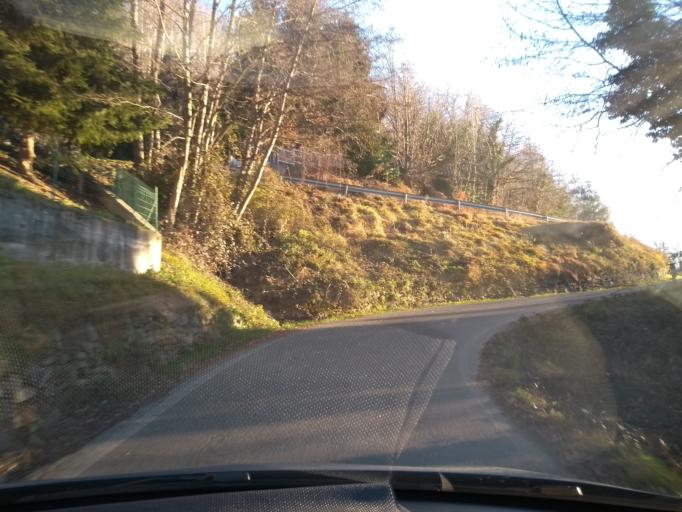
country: IT
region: Piedmont
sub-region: Provincia di Torino
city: Corio
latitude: 45.3206
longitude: 7.5323
